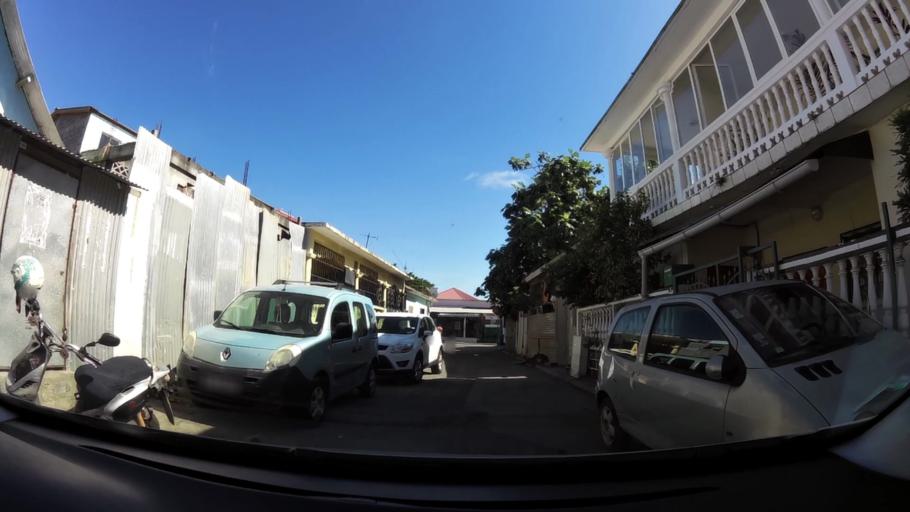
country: YT
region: Pamandzi
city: Pamandzi
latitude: -12.7874
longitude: 45.2730
